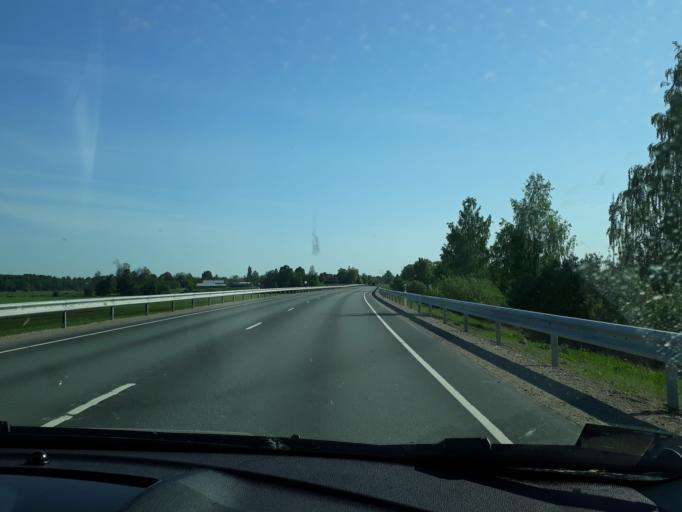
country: EE
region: Paernumaa
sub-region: Tootsi vald
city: Tootsi
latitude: 58.5244
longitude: 24.8254
